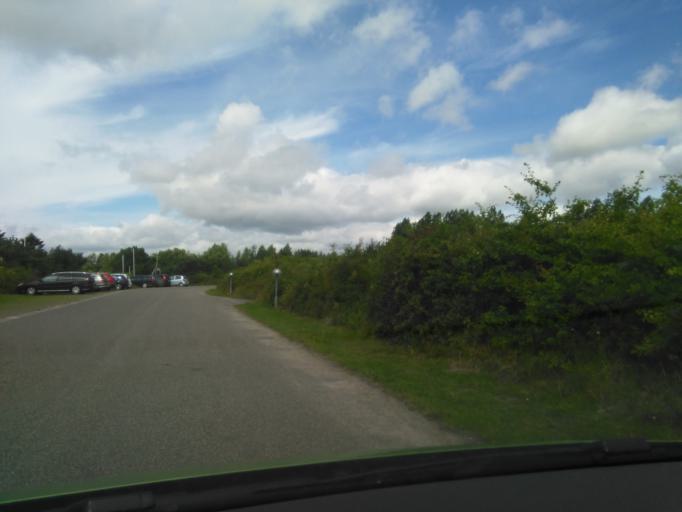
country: DK
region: Central Jutland
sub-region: Arhus Kommune
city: Logten
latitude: 56.2449
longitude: 10.3407
